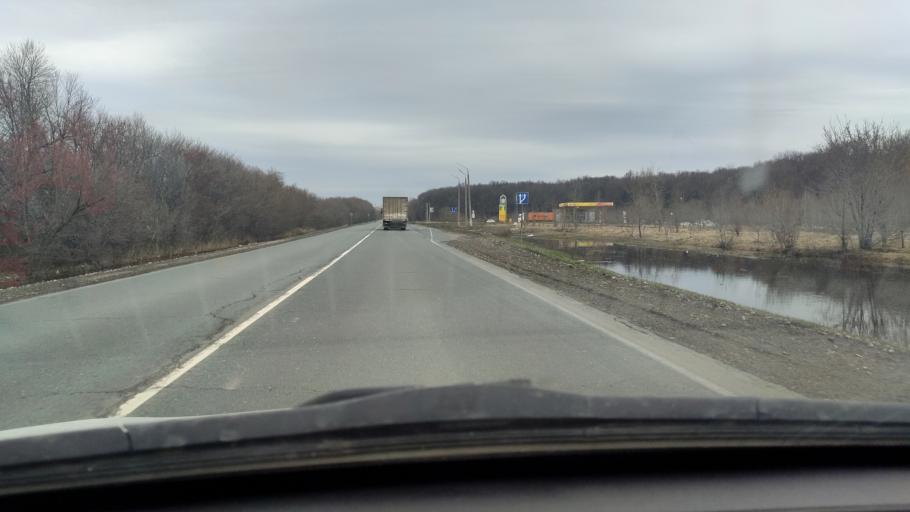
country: RU
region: Samara
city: Zhigulevsk
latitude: 53.3140
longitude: 49.3606
